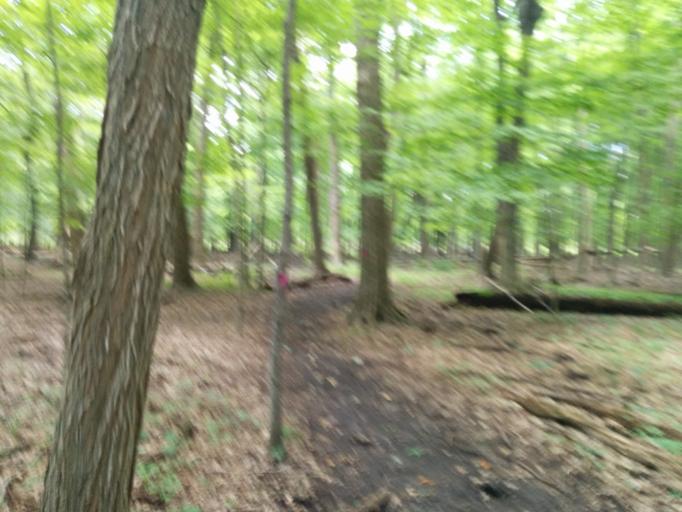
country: US
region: Illinois
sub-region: Lake County
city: Riverwoods
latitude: 42.1506
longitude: -87.9076
